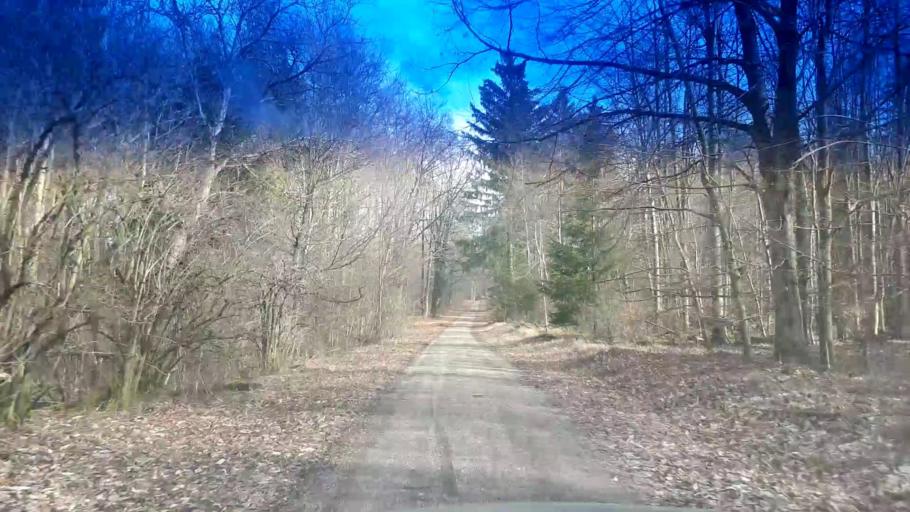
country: DE
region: Bavaria
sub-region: Upper Franconia
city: Litzendorf
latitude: 49.9367
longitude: 11.0434
